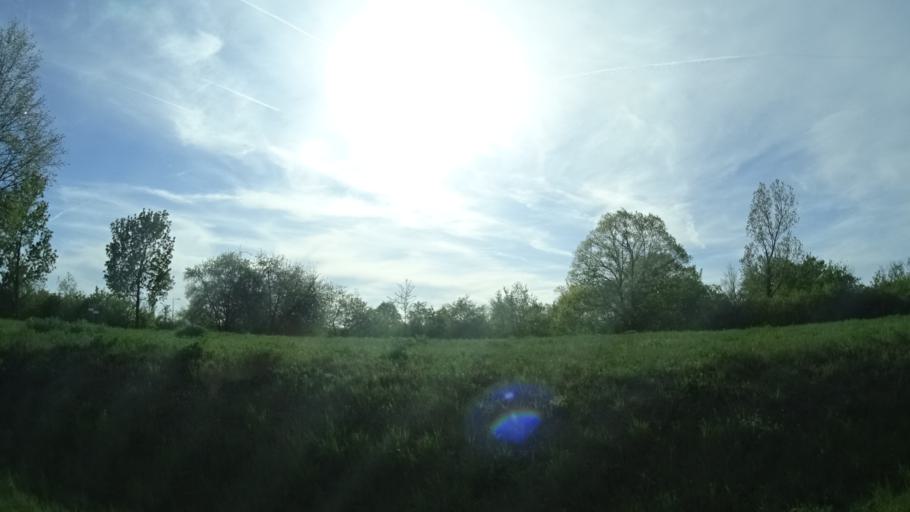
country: DE
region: Bavaria
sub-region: Regierungsbezirk Unterfranken
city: Sommerach
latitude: 49.8174
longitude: 10.2228
